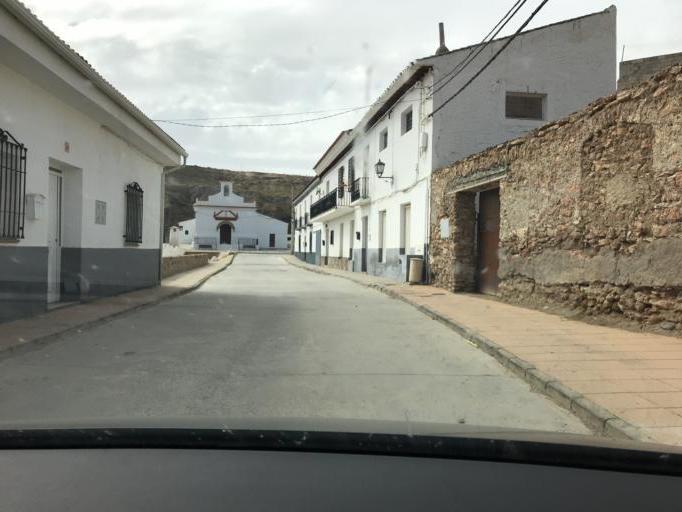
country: ES
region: Andalusia
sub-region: Provincia de Granada
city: Villanueva de las Torres
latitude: 37.4798
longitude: -3.0437
